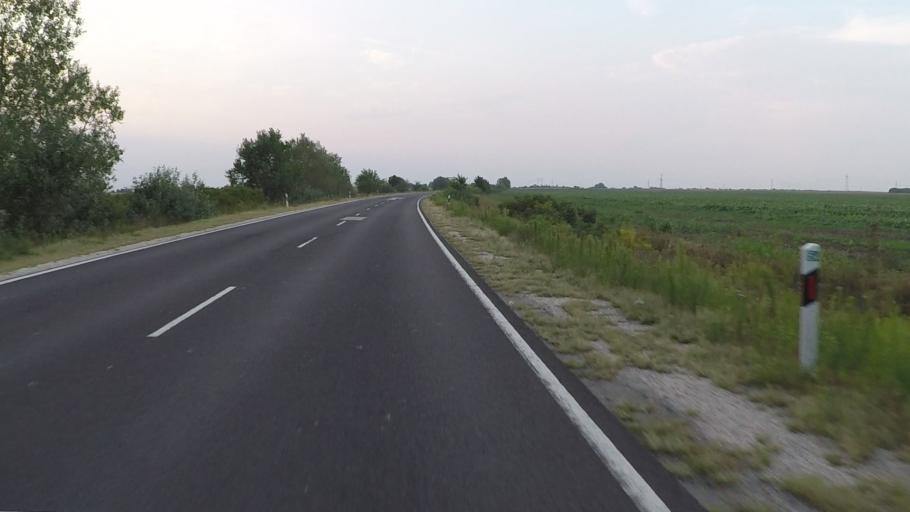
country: HU
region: Pest
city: Abony
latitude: 47.1978
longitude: 20.0802
